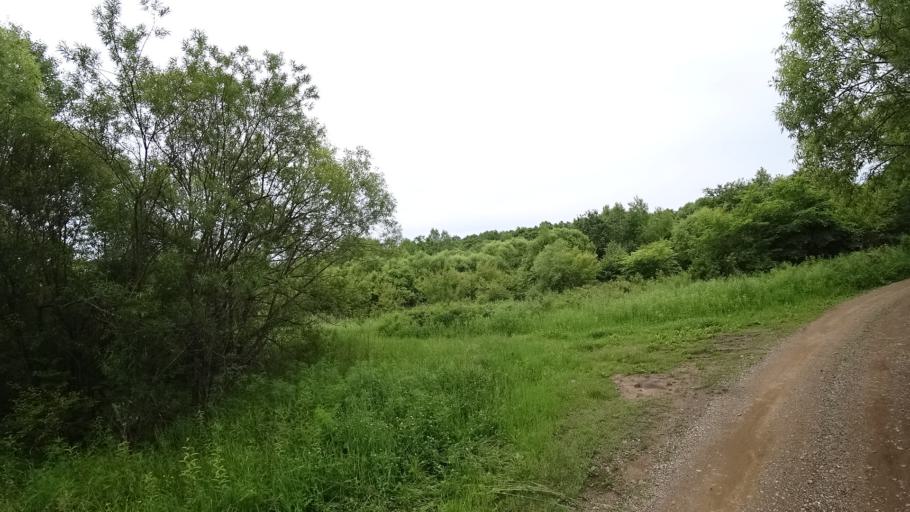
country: RU
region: Primorskiy
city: Novosysoyevka
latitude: 44.2035
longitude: 133.3275
